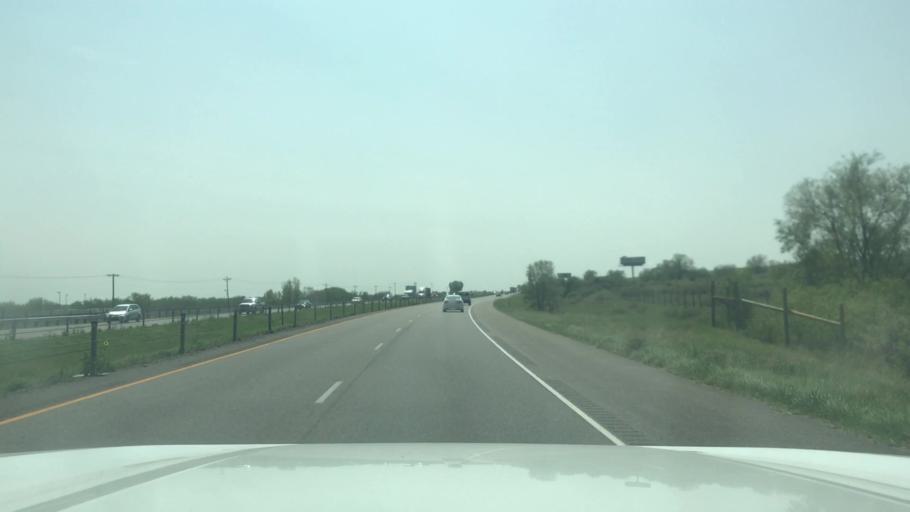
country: US
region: Colorado
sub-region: El Paso County
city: Fountain
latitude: 38.6632
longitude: -104.7018
